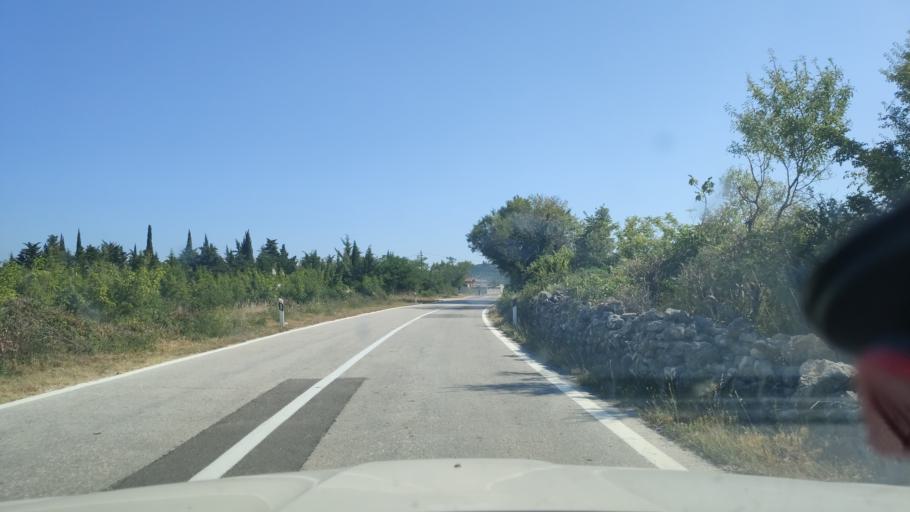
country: HR
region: Sibensko-Kniniska
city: Kistanje
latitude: 43.9605
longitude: 15.8640
